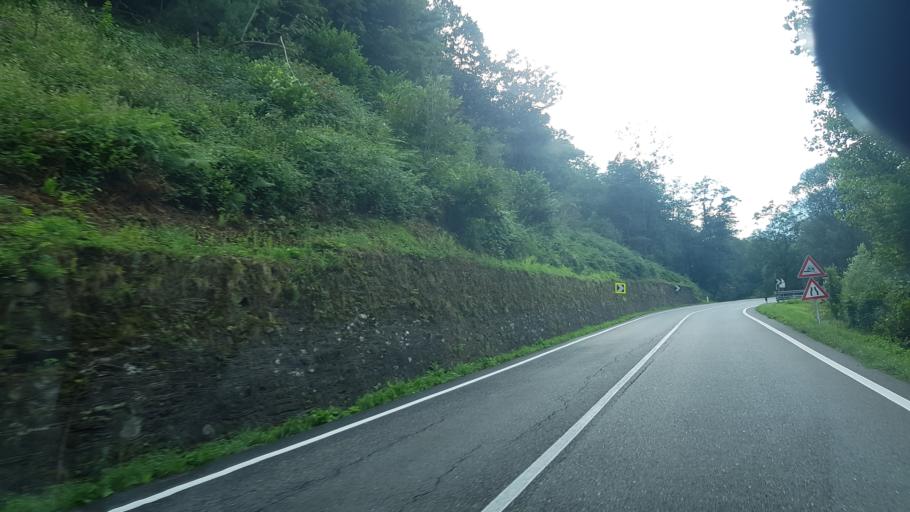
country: IT
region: Piedmont
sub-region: Provincia di Cuneo
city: Frassino
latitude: 44.5690
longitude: 7.2868
